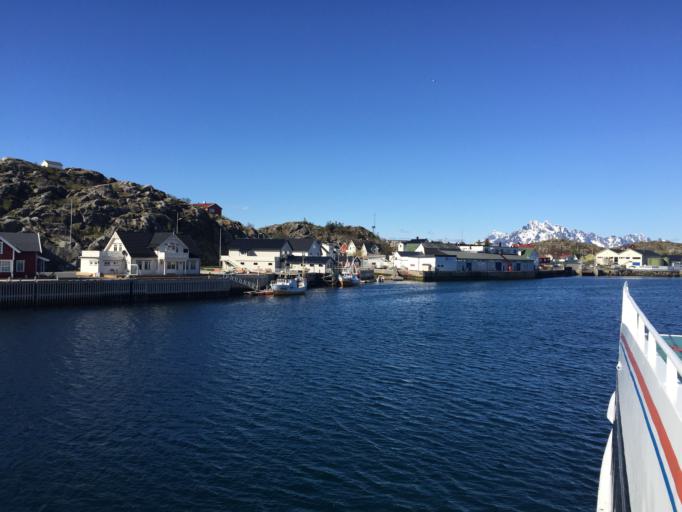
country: NO
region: Nordland
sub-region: Vagan
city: Svolvaer
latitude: 68.1644
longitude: 14.6599
